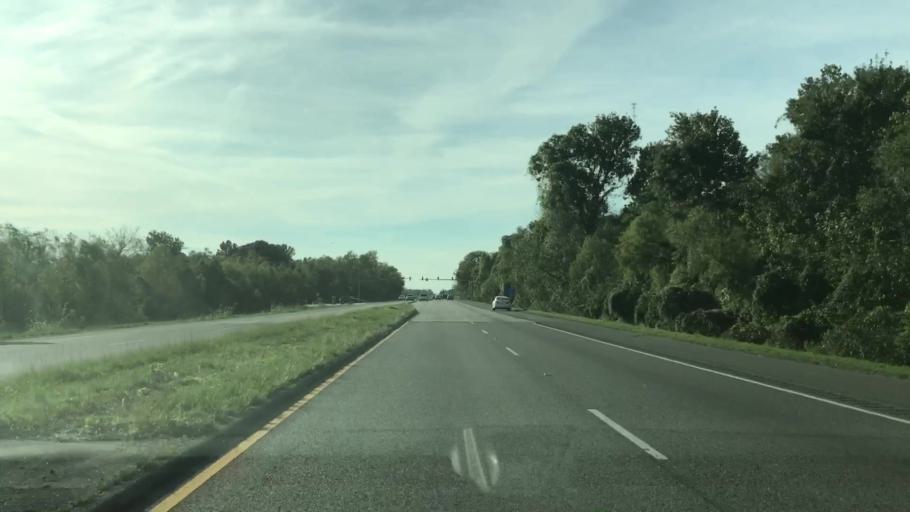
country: US
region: Louisiana
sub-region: Jefferson Parish
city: Avondale
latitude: 29.9092
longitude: -90.1894
